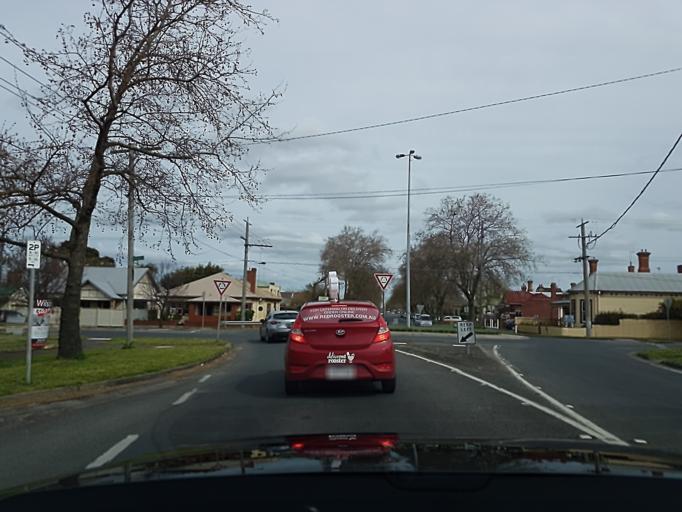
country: AU
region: Victoria
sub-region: Ballarat North
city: Ballarat Central
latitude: -37.5625
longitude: 143.8472
